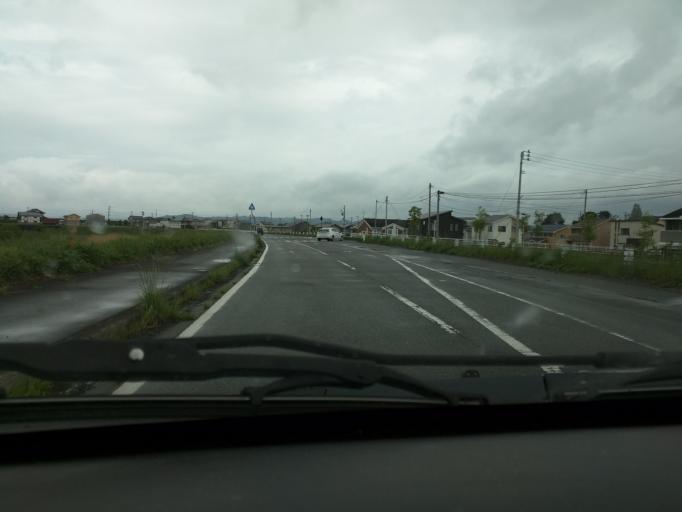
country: JP
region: Fukushima
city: Kitakata
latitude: 37.5938
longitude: 139.8836
